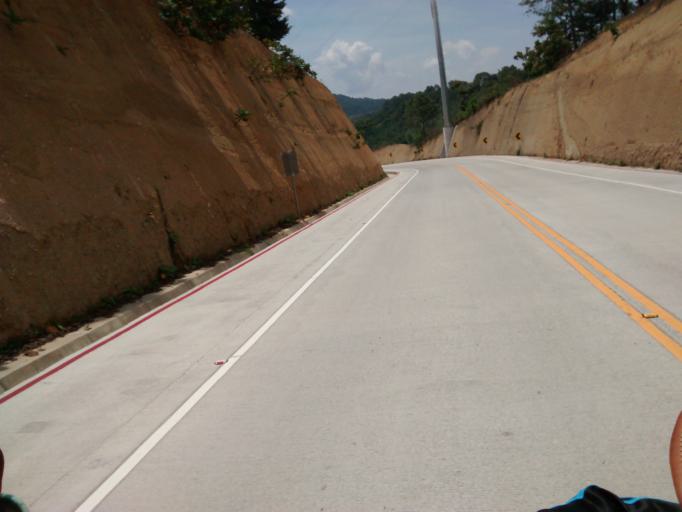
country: GT
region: Sacatepequez
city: Santo Domingo Xenacoj
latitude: 14.6819
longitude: -90.7152
